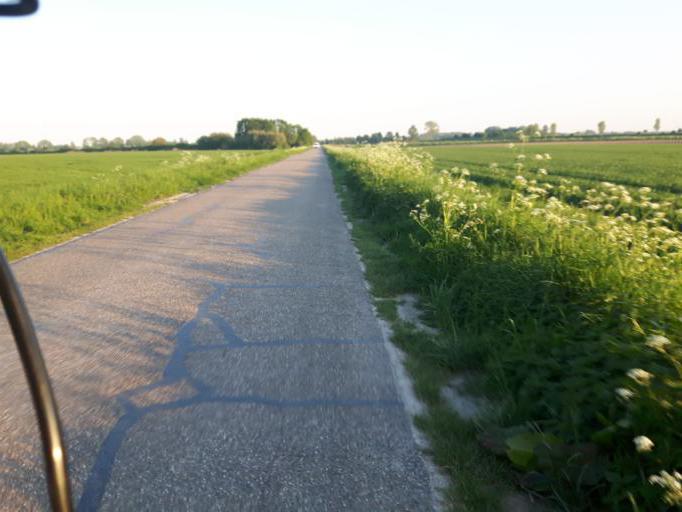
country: NL
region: Zeeland
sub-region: Gemeente Goes
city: Goes
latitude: 51.5077
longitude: 3.8083
